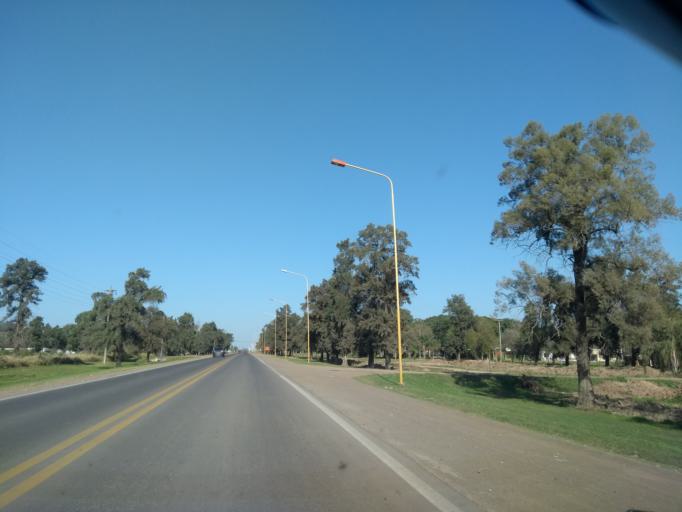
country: AR
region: Chaco
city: Presidencia Roque Saenz Pena
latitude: -26.8047
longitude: -60.4150
